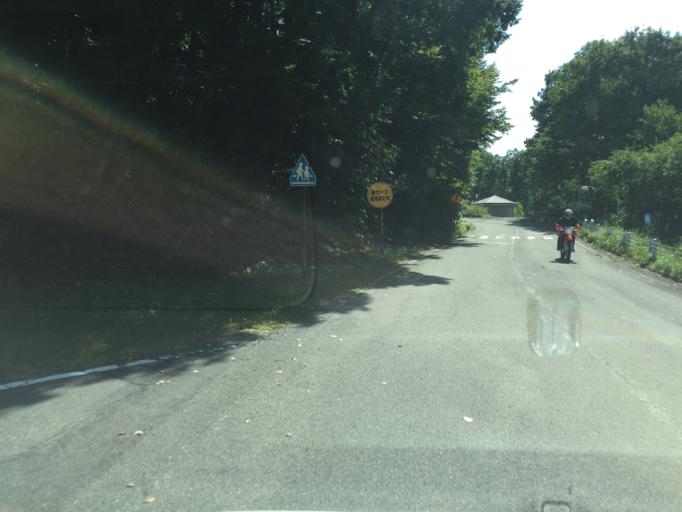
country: JP
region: Fukushima
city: Inawashiro
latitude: 37.6559
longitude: 140.1619
